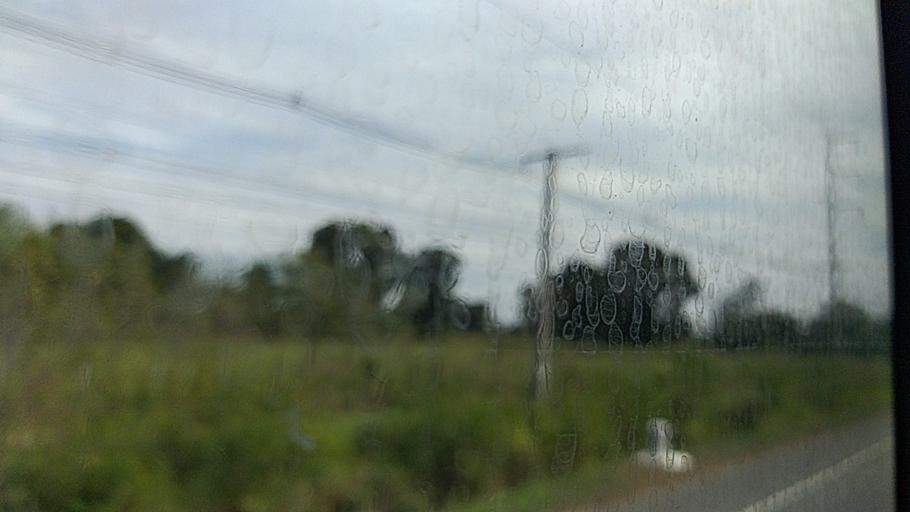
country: TH
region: Maha Sarakham
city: Chiang Yuen
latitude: 16.4348
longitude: 103.0540
